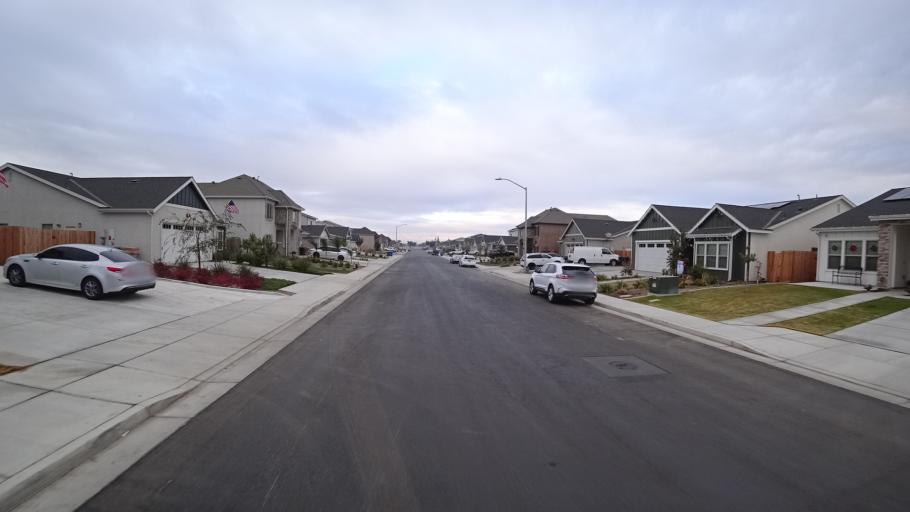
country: US
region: California
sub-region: Kern County
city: Greenfield
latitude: 35.2926
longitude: -119.0663
